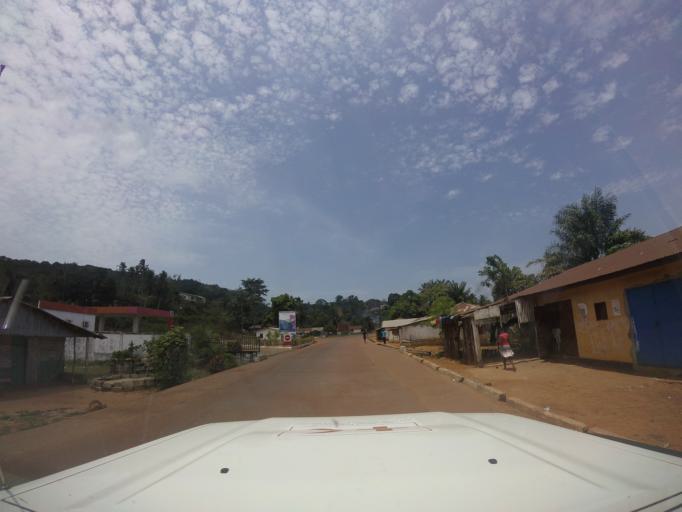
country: LR
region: Grand Cape Mount
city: Robertsport
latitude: 6.7544
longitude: -11.3636
